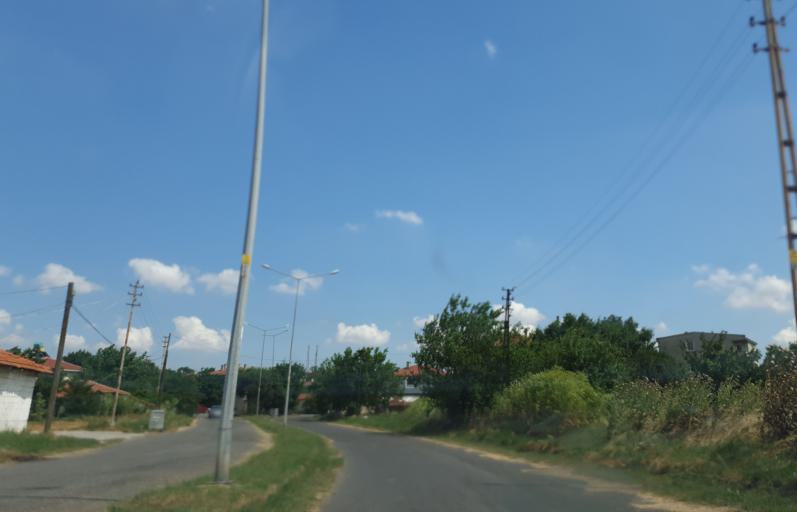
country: TR
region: Tekirdag
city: Muratli
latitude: 41.2178
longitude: 27.5448
